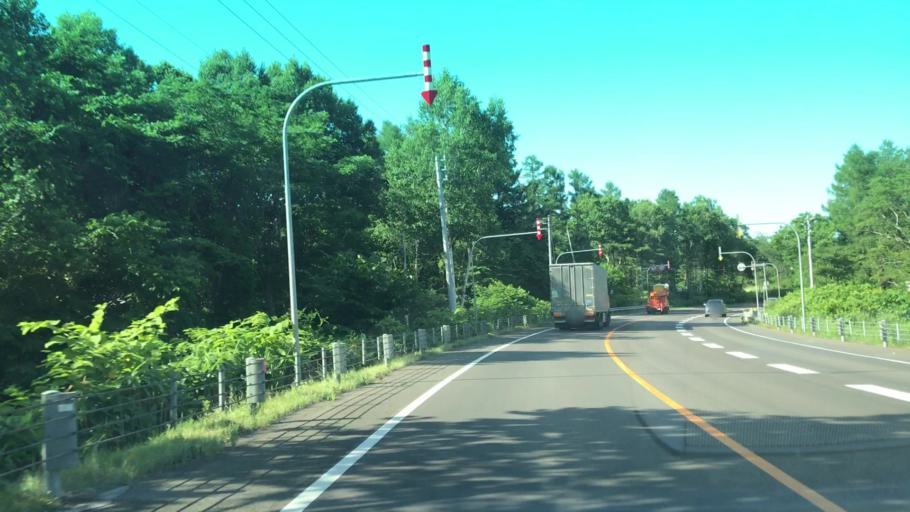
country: JP
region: Hokkaido
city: Yoichi
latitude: 43.0714
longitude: 140.6992
